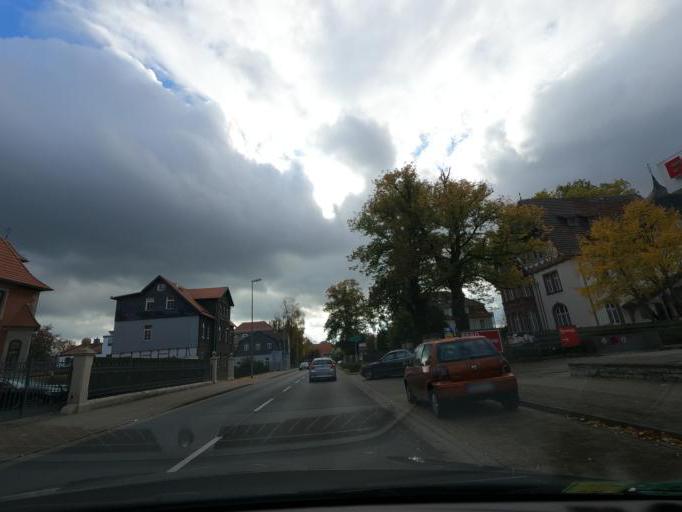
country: DE
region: Lower Saxony
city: Wolfenbuettel
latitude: 52.1701
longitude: 10.5414
